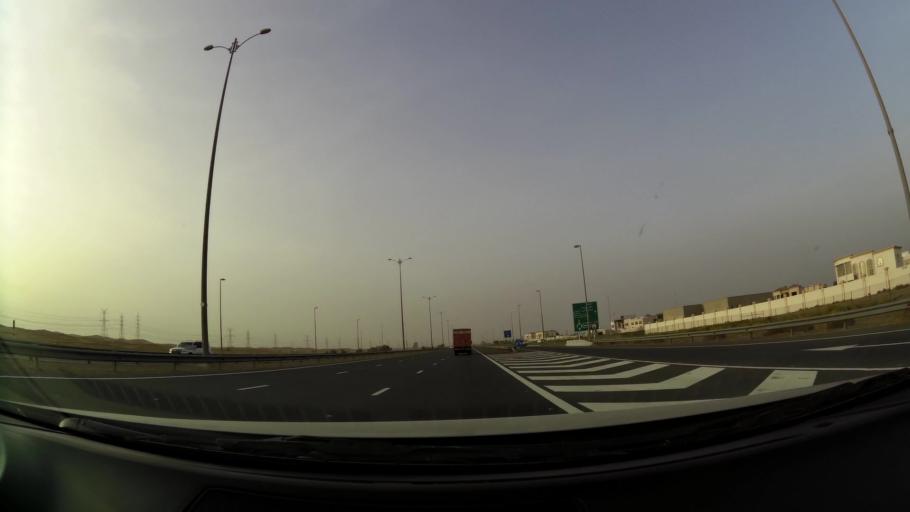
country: OM
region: Al Buraimi
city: Al Buraymi
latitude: 24.2898
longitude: 55.7358
